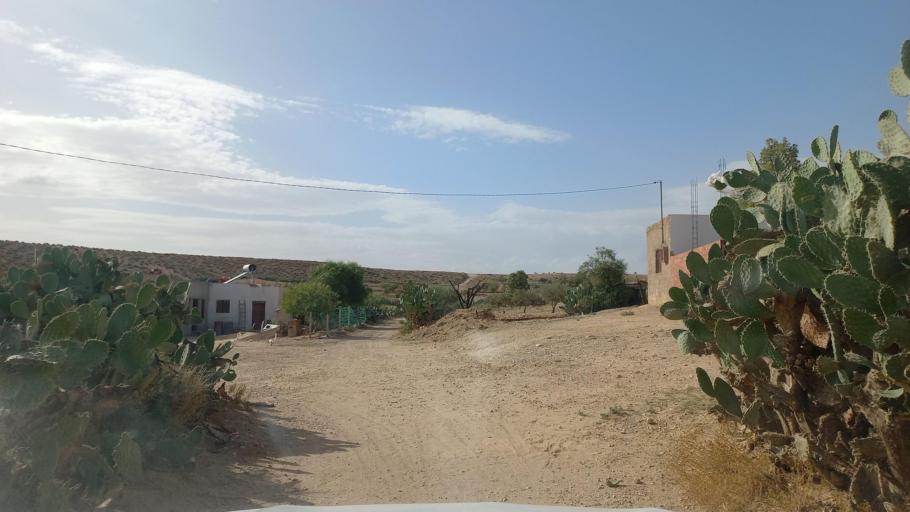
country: TN
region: Al Qasrayn
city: Kasserine
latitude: 35.2582
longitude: 8.9284
